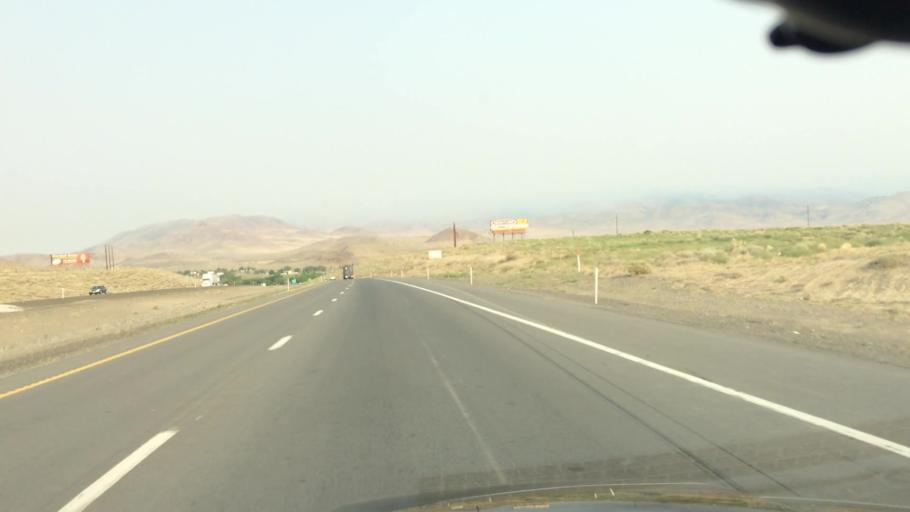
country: US
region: Nevada
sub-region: Lyon County
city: Fernley
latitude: 39.6181
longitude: -119.2784
